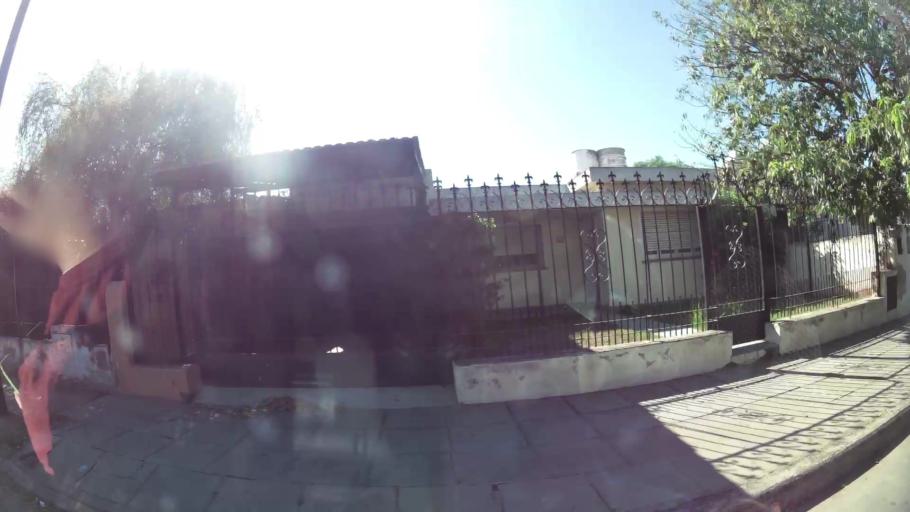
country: AR
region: Cordoba
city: Villa Allende
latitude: -31.3438
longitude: -64.2419
